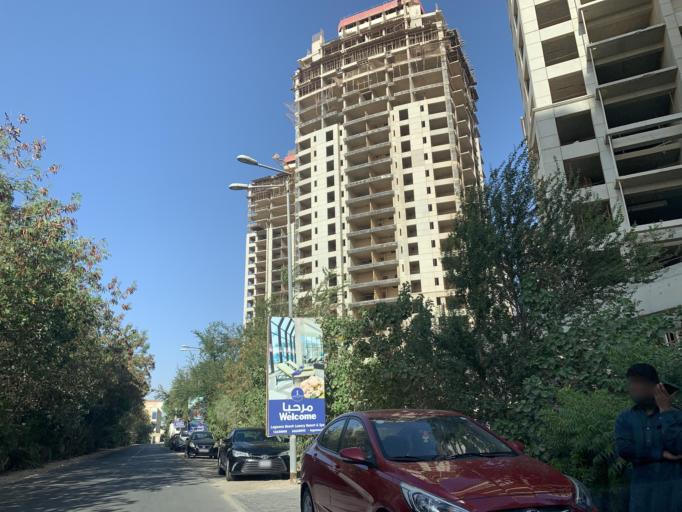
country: BH
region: Manama
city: Jidd Hafs
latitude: 26.2039
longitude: 50.4499
